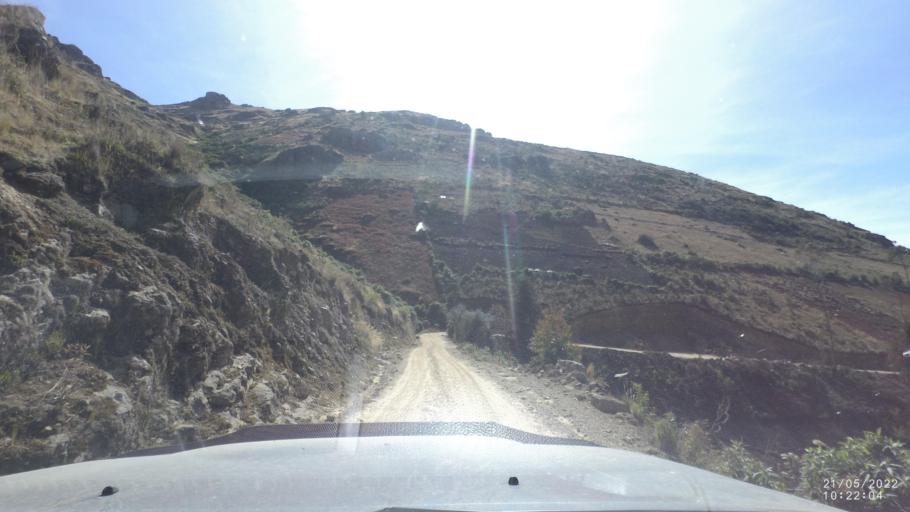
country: BO
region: Cochabamba
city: Colomi
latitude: -17.3248
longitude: -65.9558
